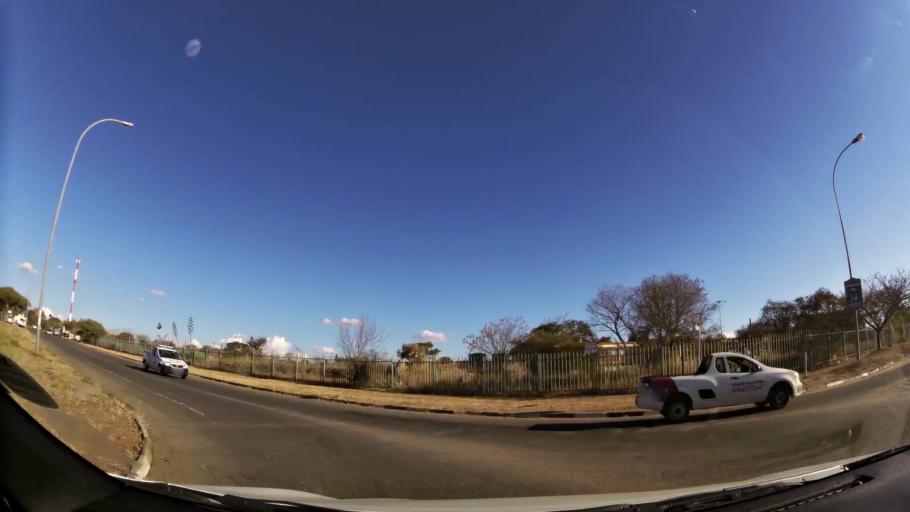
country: ZA
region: Limpopo
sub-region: Capricorn District Municipality
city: Polokwane
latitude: -23.8901
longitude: 29.4614
